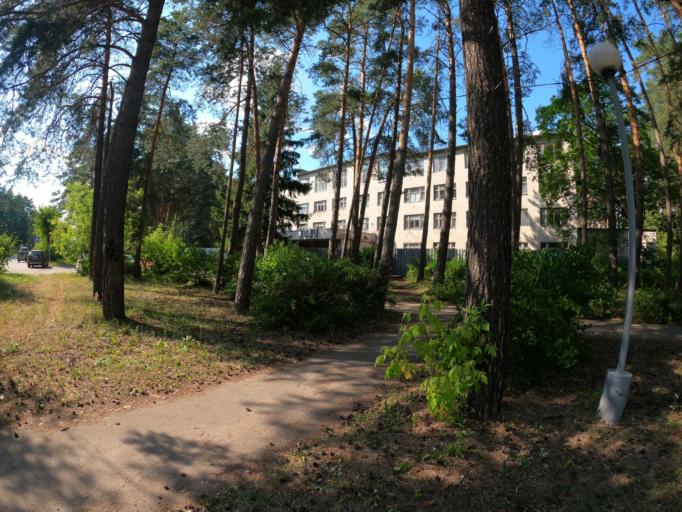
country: RU
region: Moskovskaya
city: Protvino
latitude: 54.8657
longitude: 37.2104
